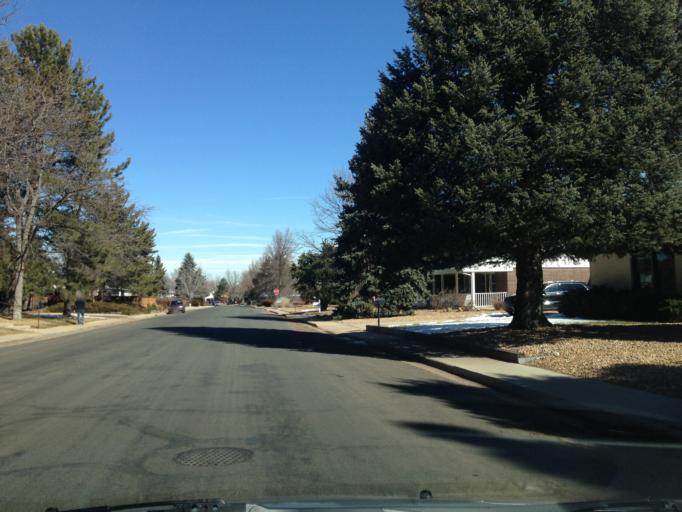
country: US
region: Colorado
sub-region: Boulder County
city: Boulder
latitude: 39.9870
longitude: -105.2275
